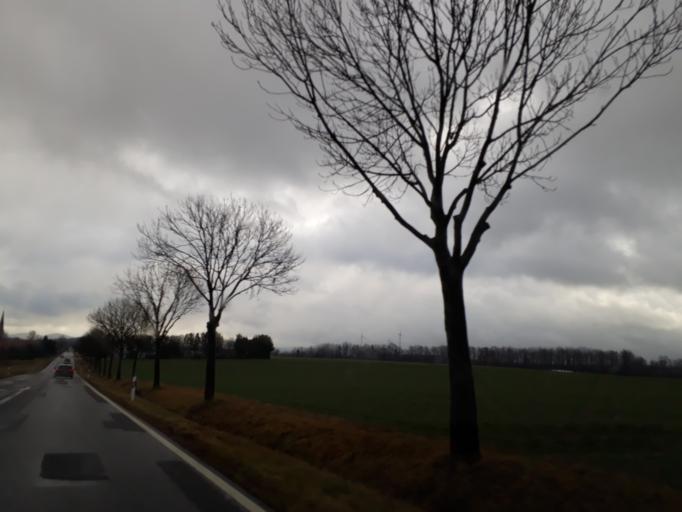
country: DE
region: Saxony
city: Herrnhut
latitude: 51.0338
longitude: 14.7154
